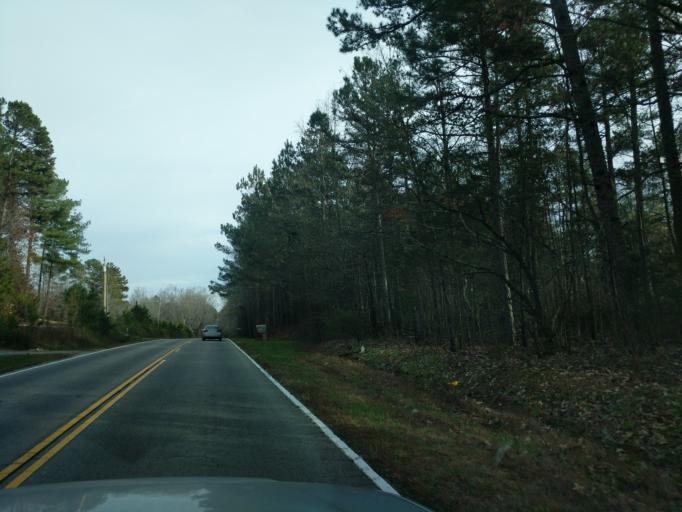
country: US
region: South Carolina
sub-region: Pickens County
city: Liberty
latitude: 34.7065
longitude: -82.7010
